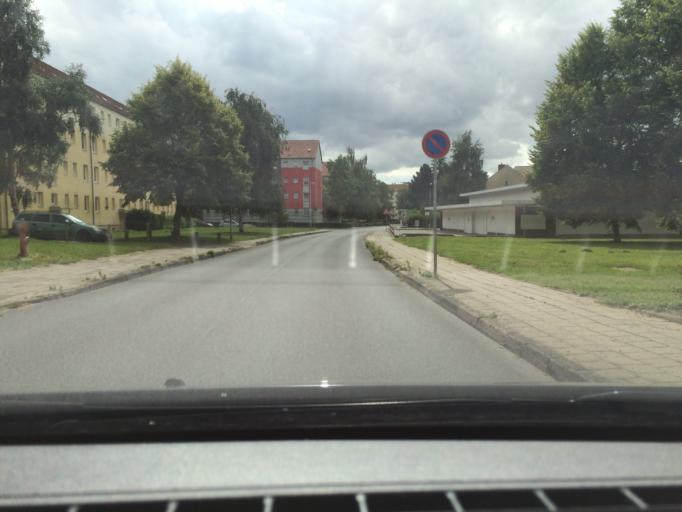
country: DE
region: Mecklenburg-Vorpommern
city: Stralsund
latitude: 54.3275
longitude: 13.0713
